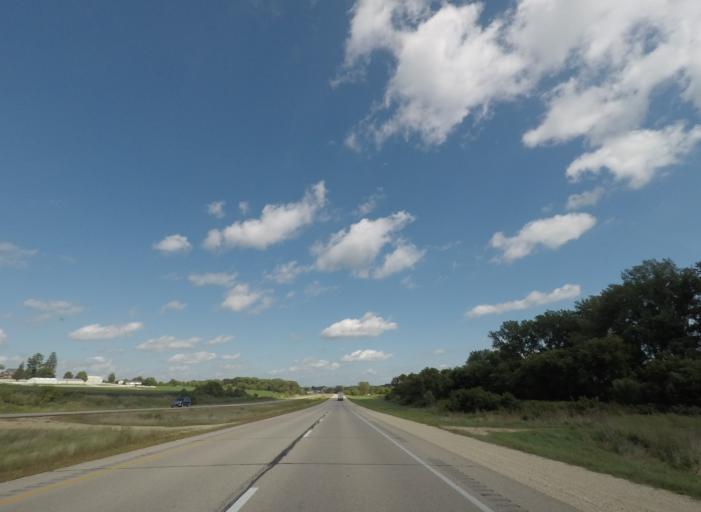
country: US
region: Iowa
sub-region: Dubuque County
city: Cascade
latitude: 42.3168
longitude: -90.9349
